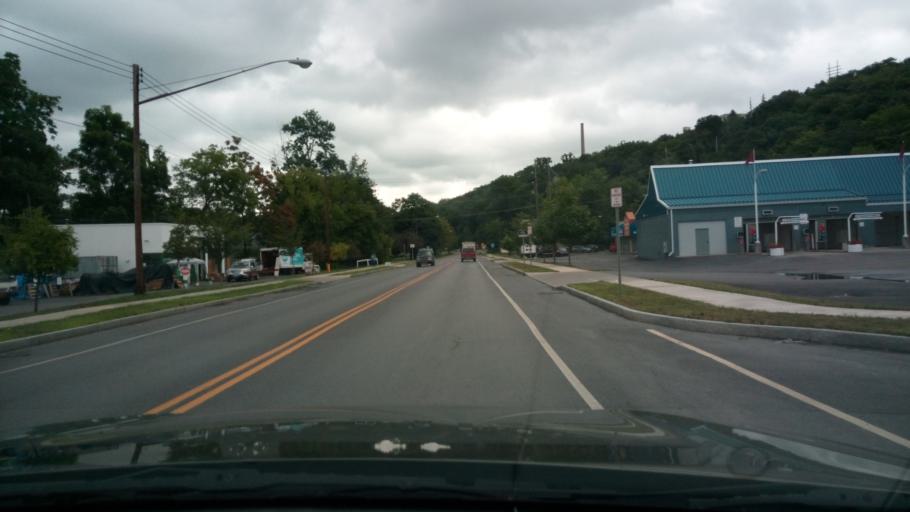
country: US
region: New York
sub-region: Tompkins County
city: South Hill
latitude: 42.4300
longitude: -76.5046
